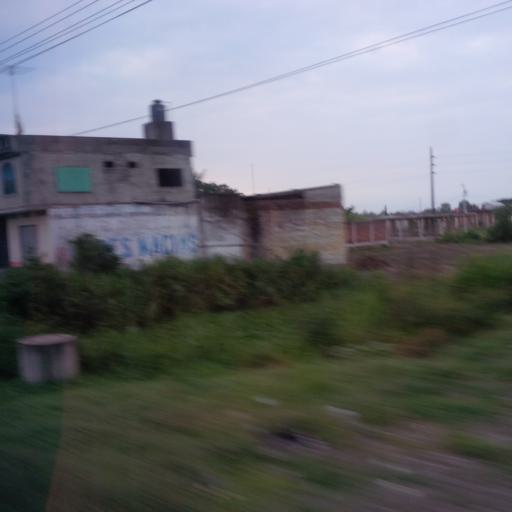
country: EC
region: Guayas
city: Coronel Marcelino Mariduena
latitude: -2.3277
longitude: -79.4142
